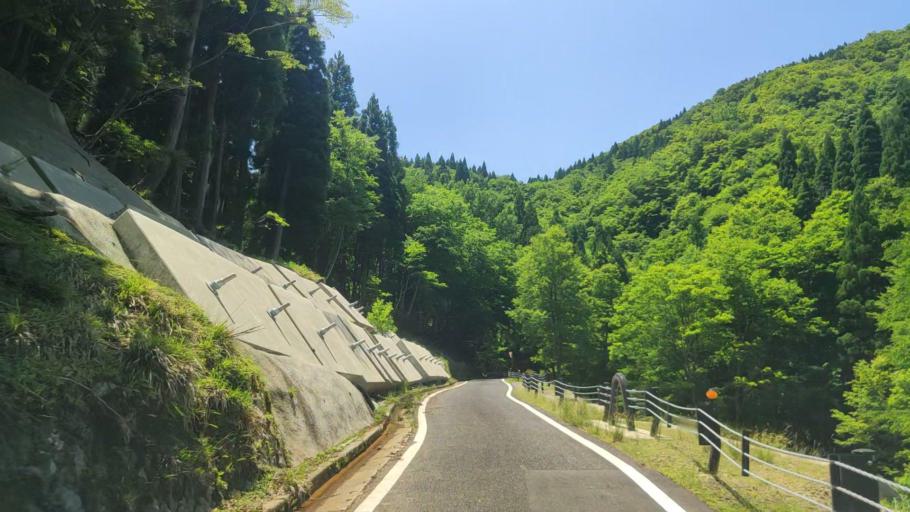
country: JP
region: Tottori
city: Tottori
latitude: 35.3724
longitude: 134.4910
